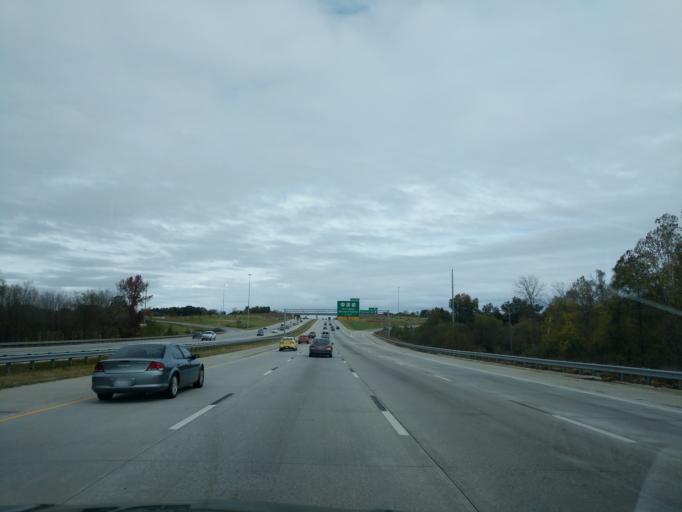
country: US
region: North Carolina
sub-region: Davidson County
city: Tyro
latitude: 35.7488
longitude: -80.3529
